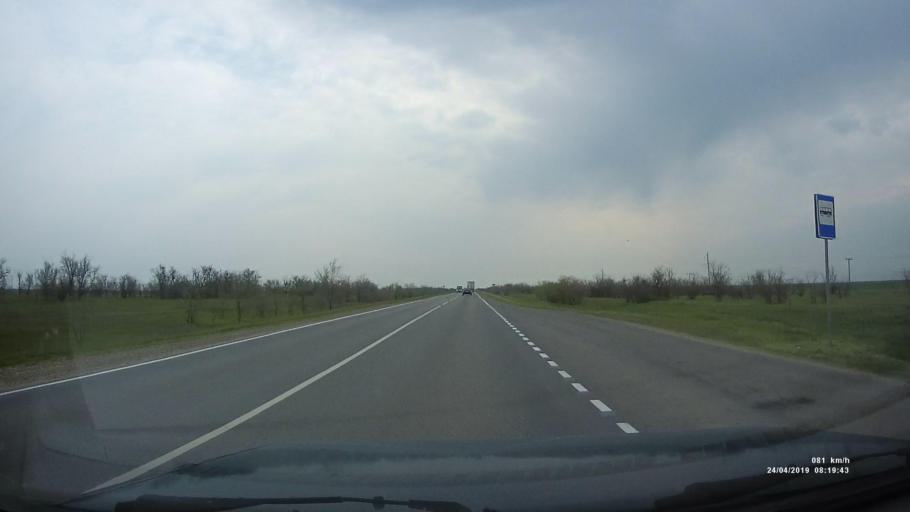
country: RU
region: Kalmykiya
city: Priyutnoye
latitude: 46.1050
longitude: 43.6702
